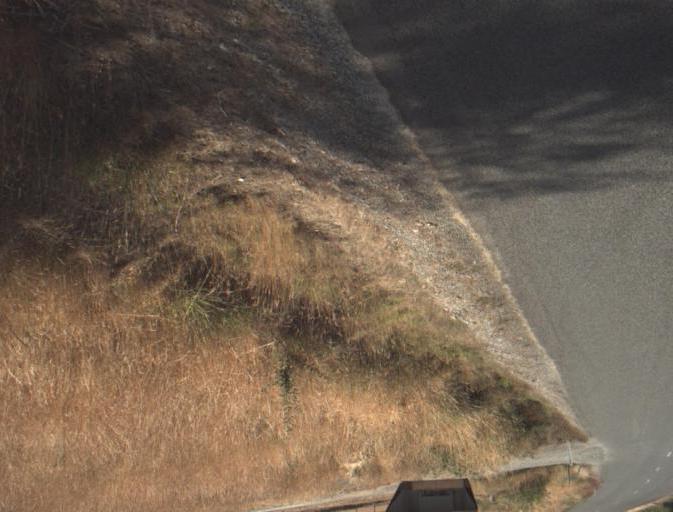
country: AU
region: Tasmania
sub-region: Launceston
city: Mayfield
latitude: -41.1868
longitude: 147.2220
